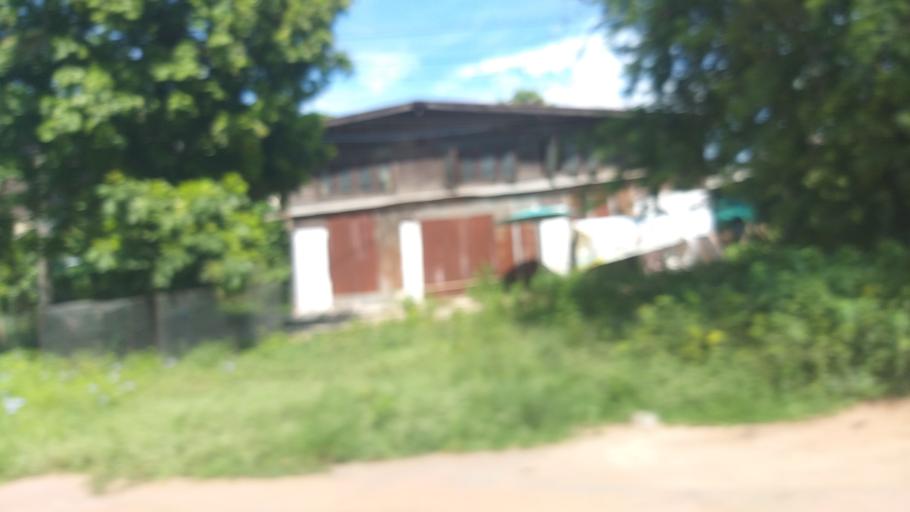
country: TH
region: Khon Kaen
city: Nong Ruea
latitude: 16.4874
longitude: 102.4349
